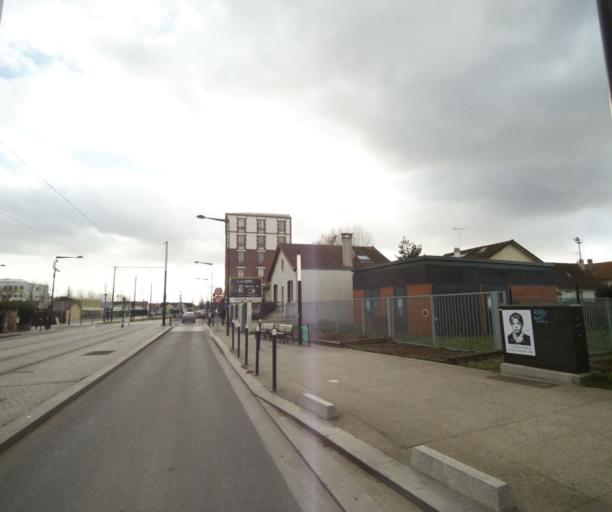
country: FR
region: Ile-de-France
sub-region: Departement de Seine-Saint-Denis
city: Villetaneuse
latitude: 48.9540
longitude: 2.3437
